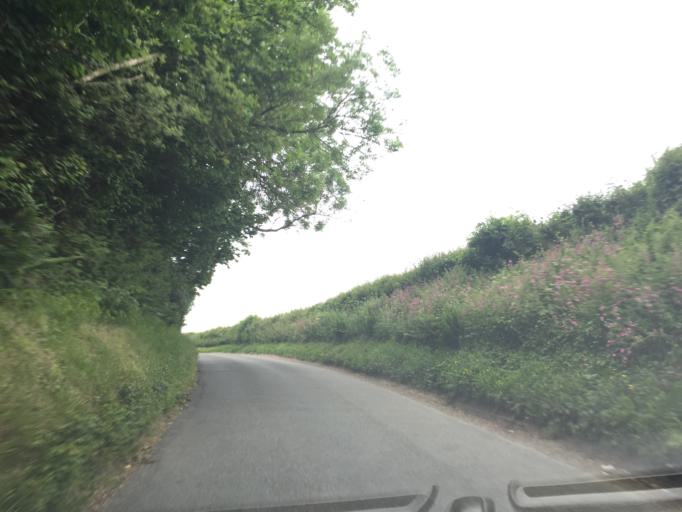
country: GB
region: England
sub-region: Dorset
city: Dorchester
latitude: 50.7215
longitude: -2.3920
